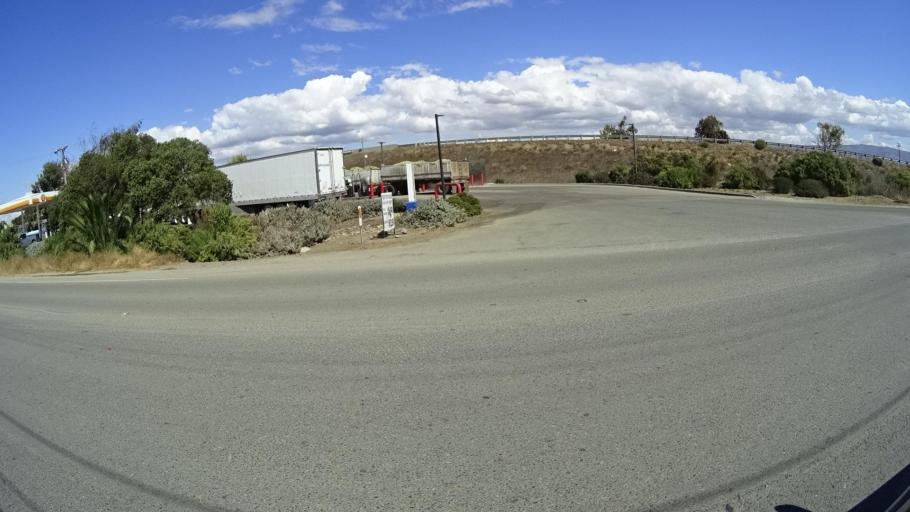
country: US
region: California
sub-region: Monterey County
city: Gonzales
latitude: 36.5213
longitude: -121.4663
